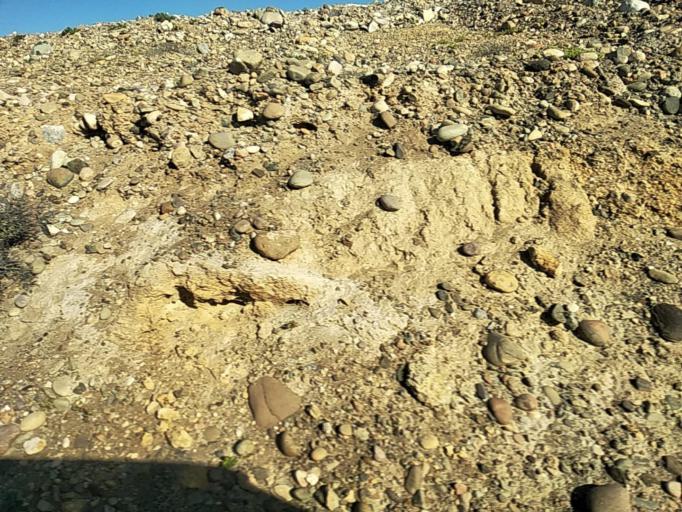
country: CL
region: Atacama
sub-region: Provincia de Copiapo
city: Copiapo
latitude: -27.3276
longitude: -70.7796
